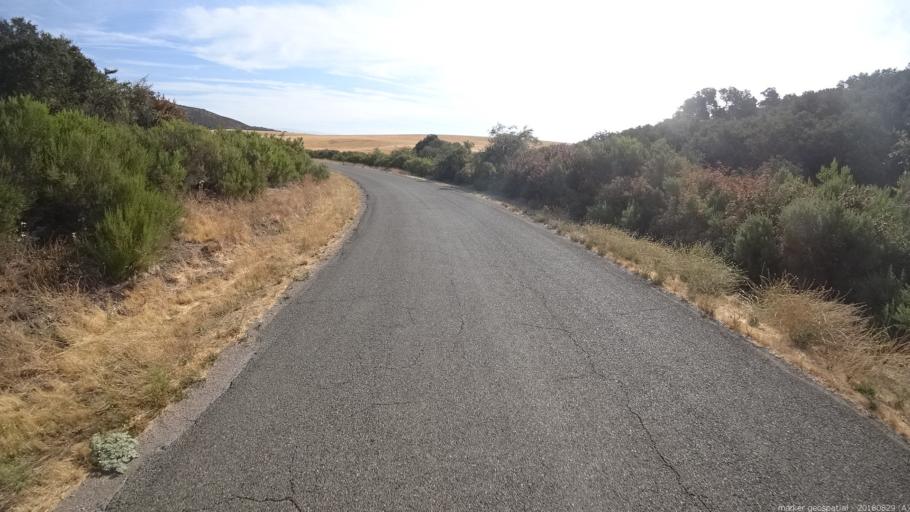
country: US
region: California
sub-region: Monterey County
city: King City
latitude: 36.0475
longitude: -121.0534
